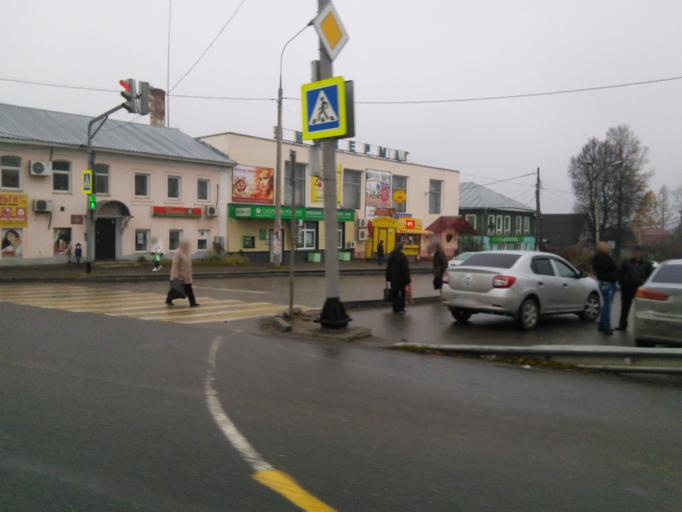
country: RU
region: Jaroslavl
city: Petrovsk
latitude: 57.0134
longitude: 39.2635
